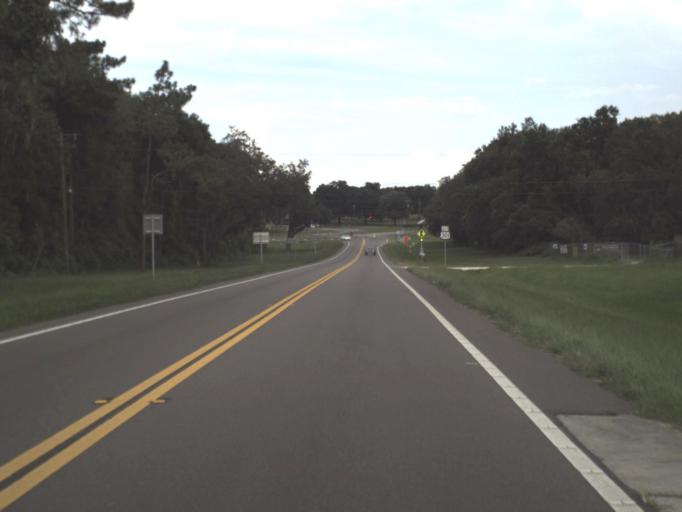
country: US
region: Florida
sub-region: Pasco County
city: Dade City
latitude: 28.3220
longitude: -82.1849
